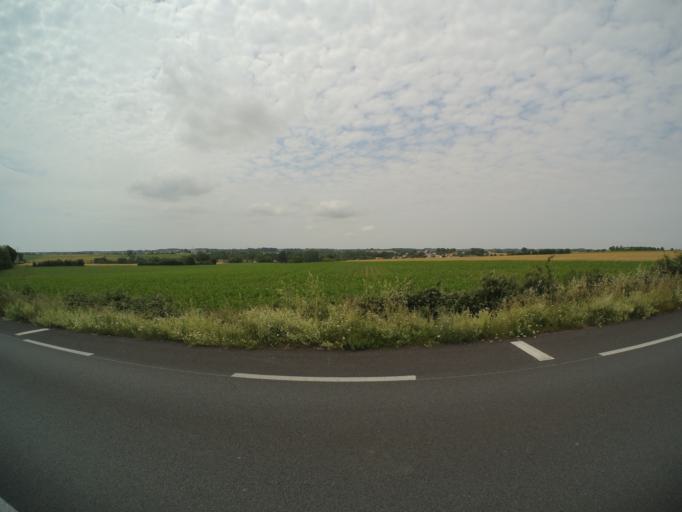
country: FR
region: Pays de la Loire
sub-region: Departement de la Vendee
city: Chavagnes-en-Paillers
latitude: 46.9083
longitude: -1.2368
